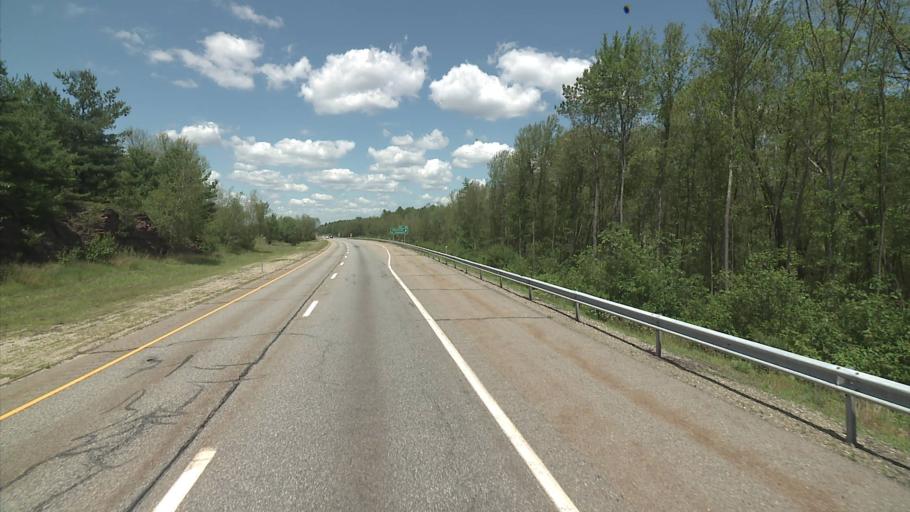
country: US
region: Connecticut
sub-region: Windham County
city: Thompson
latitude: 42.0033
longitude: -71.8526
